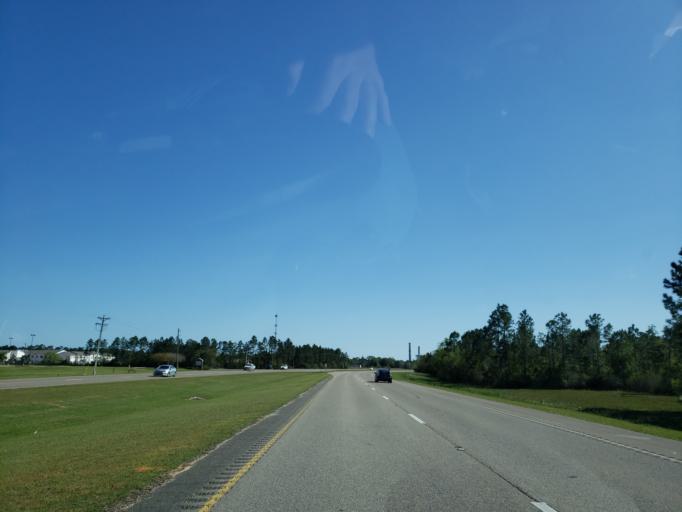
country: US
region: Mississippi
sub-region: Harrison County
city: West Gulfport
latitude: 30.4636
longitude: -89.0271
